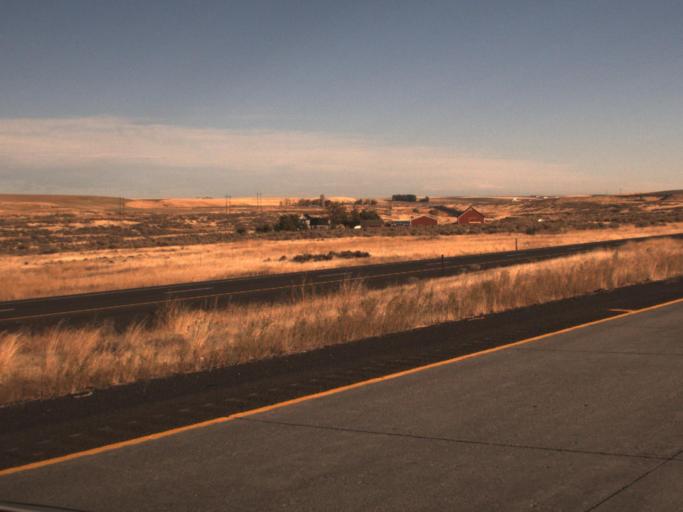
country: US
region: Washington
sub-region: Adams County
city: Ritzville
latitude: 47.0611
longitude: -118.4125
